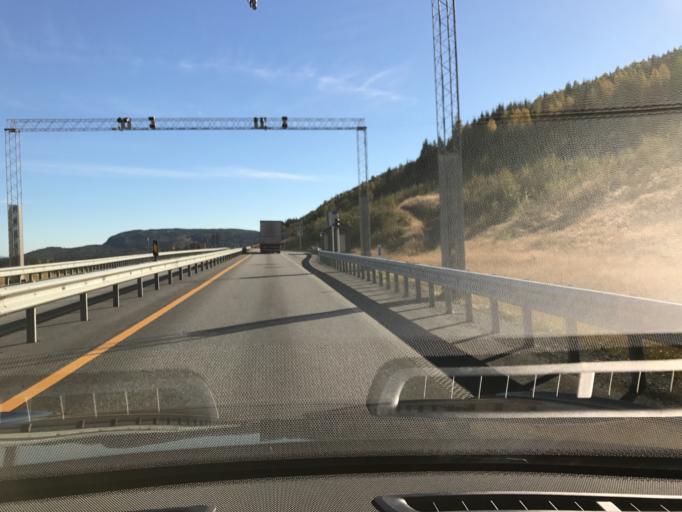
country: NO
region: Buskerud
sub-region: Krodsherad
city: Noresund
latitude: 60.2862
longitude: 9.7492
